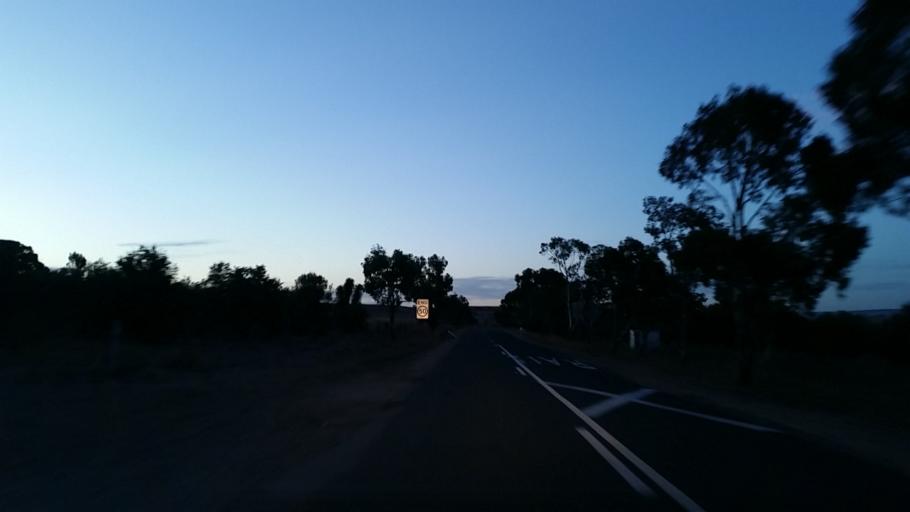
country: AU
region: South Australia
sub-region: Mount Barker
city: Callington
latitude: -35.1104
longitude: 139.0381
